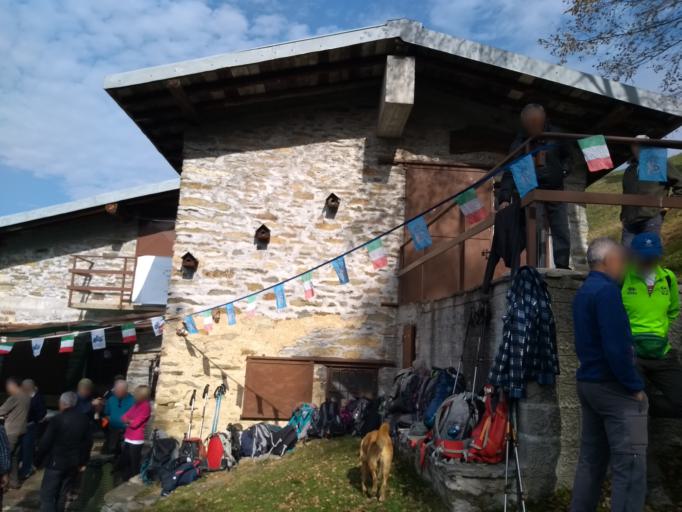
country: IT
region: Piedmont
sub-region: Provincia di Torino
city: Ceres
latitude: 45.3247
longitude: 7.4144
